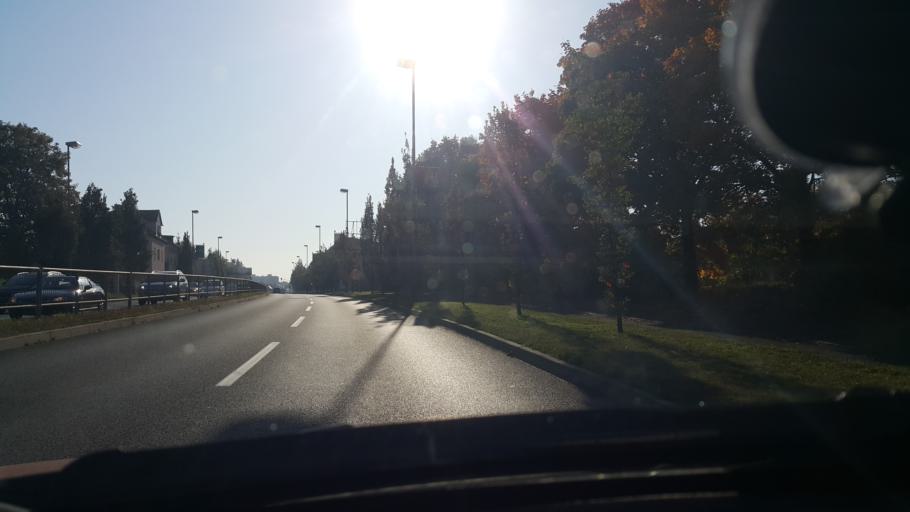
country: SI
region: Maribor
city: Maribor
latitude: 46.5381
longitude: 15.6556
